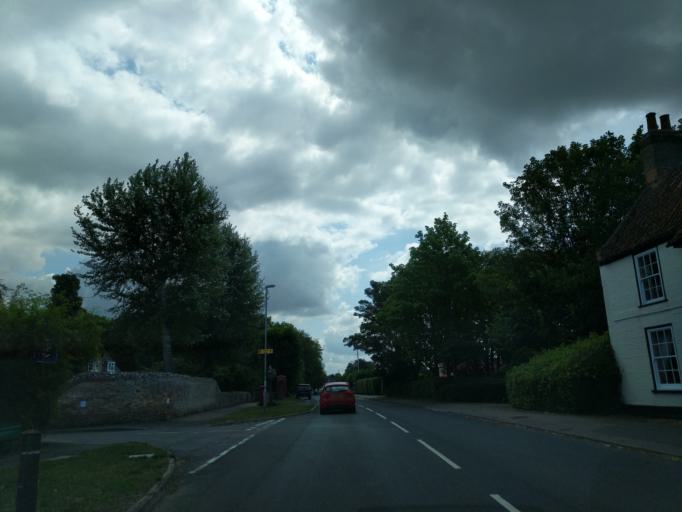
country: GB
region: England
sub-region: Cambridgeshire
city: Isleham
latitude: 52.3018
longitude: 0.4365
